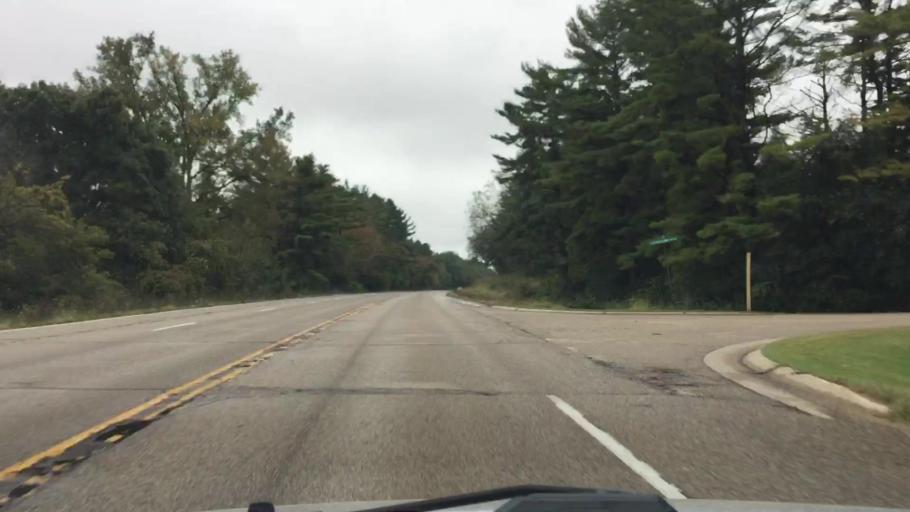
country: US
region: Wisconsin
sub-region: Rock County
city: Janesville
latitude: 42.7185
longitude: -89.0312
